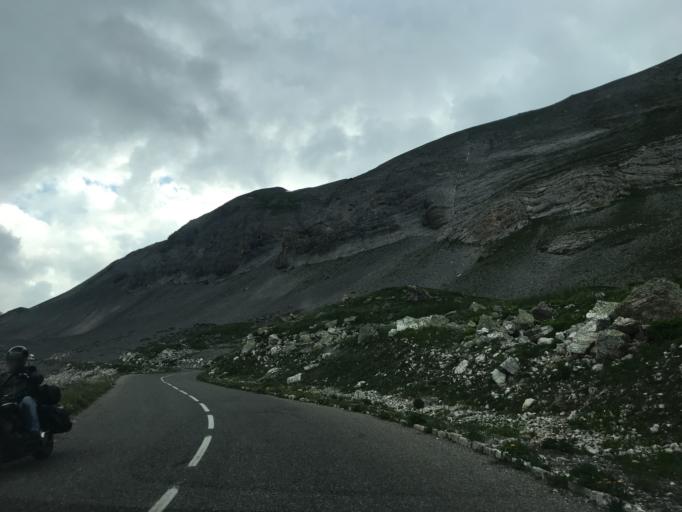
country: FR
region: Rhone-Alpes
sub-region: Departement de la Savoie
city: Valloire
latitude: 45.0850
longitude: 6.4293
